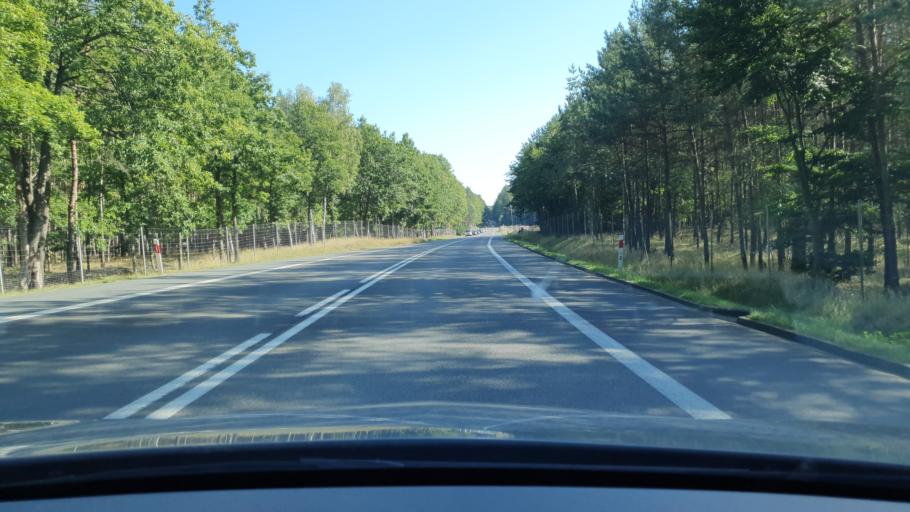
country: PL
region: West Pomeranian Voivodeship
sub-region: Powiat kamienski
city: Miedzyzdroje
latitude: 53.8898
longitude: 14.4962
